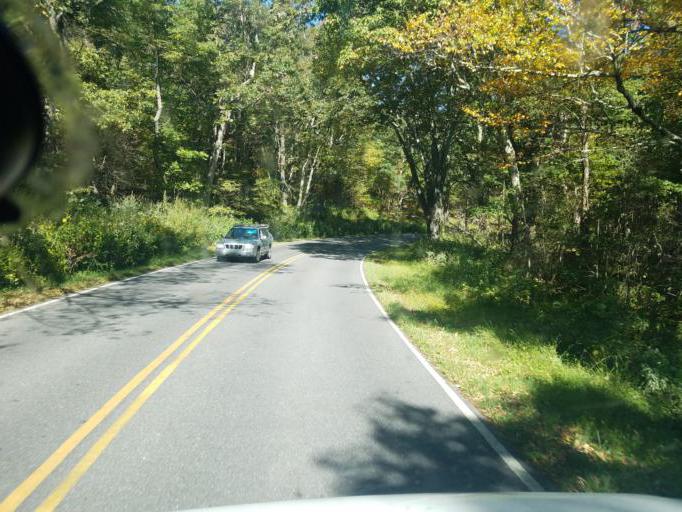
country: US
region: Virginia
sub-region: Greene County
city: Stanardsville
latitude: 38.4085
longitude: -78.4923
